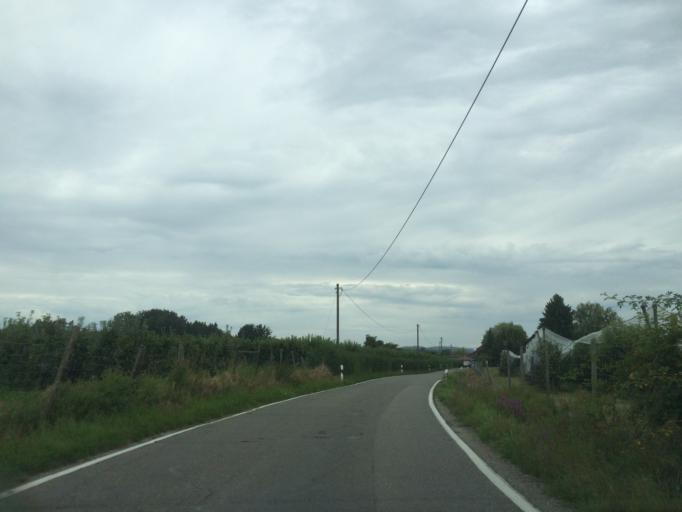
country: DE
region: Baden-Wuerttemberg
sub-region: Tuebingen Region
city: Immenstaad am Bodensee
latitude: 47.6911
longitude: 9.3483
